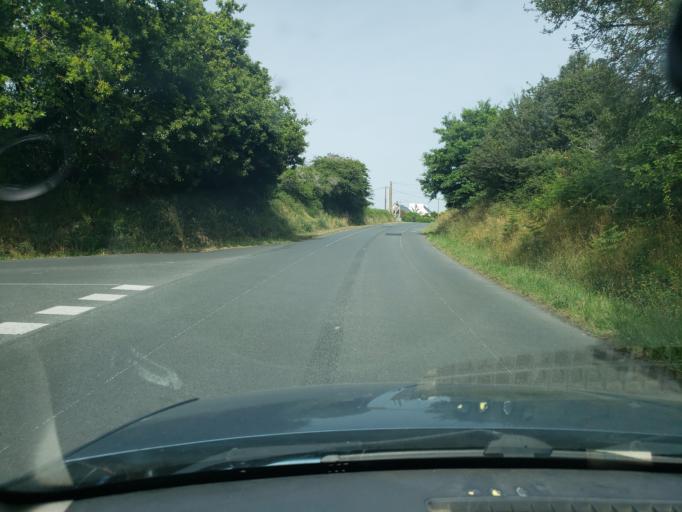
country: FR
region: Brittany
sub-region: Departement du Finistere
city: Plobannalec-Lesconil
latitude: 47.8169
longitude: -4.2336
